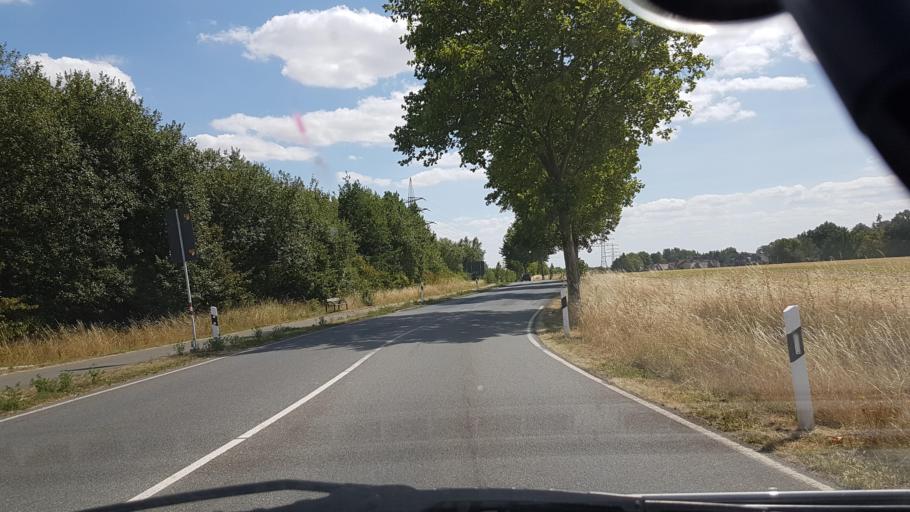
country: DE
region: Lower Saxony
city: Schoningen
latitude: 52.1495
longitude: 10.9731
